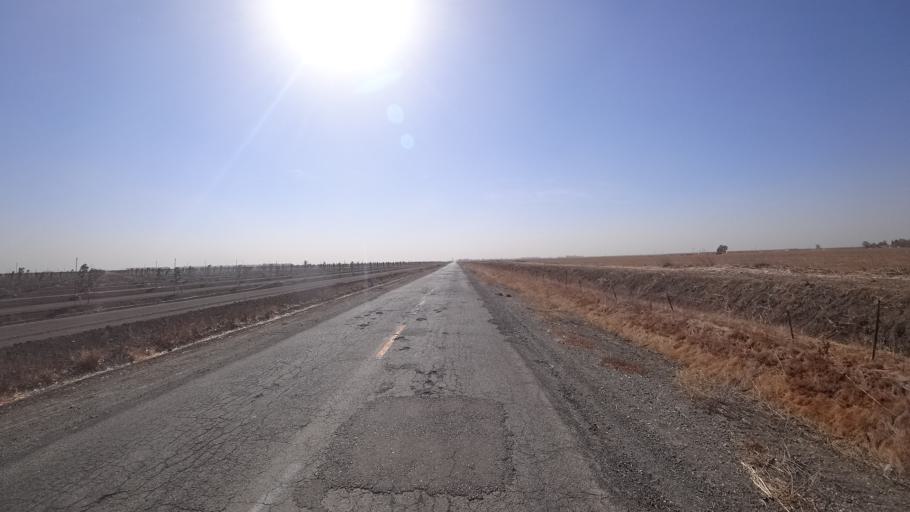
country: US
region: California
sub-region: Yolo County
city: Davis
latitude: 38.4794
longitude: -121.6930
